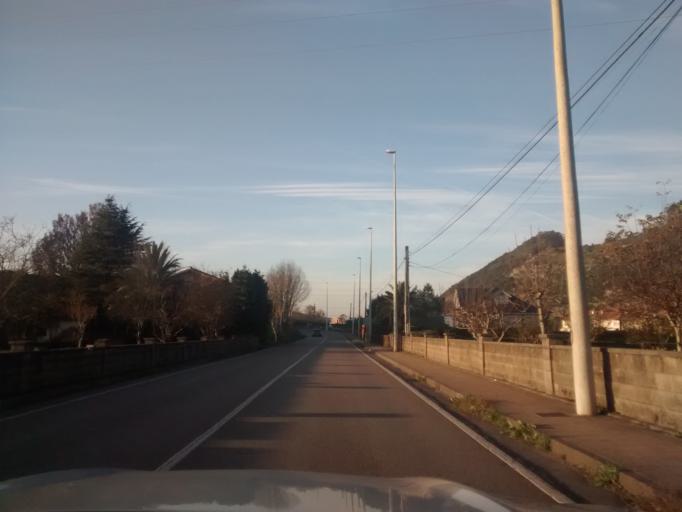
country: ES
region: Cantabria
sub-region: Provincia de Cantabria
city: Entrambasaguas
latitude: 43.3765
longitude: -3.7204
